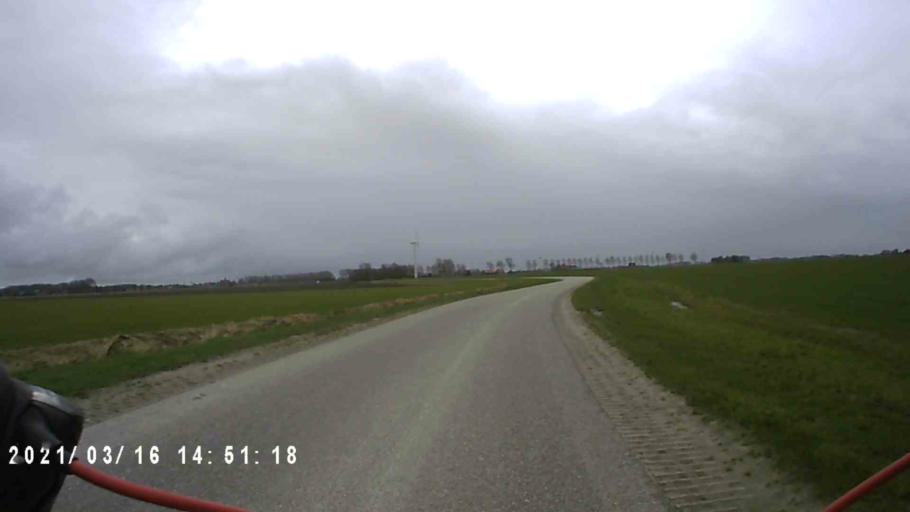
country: NL
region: Friesland
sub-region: Gemeente Harlingen
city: Harlingen
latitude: 53.1167
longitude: 5.4652
